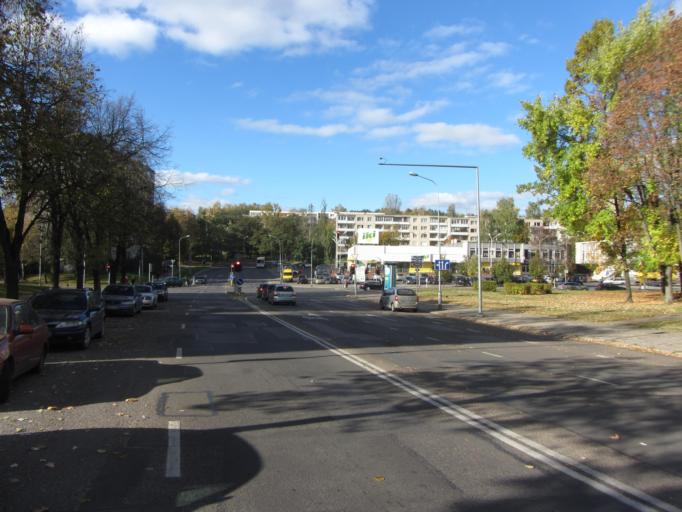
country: LT
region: Vilnius County
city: Lazdynai
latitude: 54.6736
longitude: 25.2027
